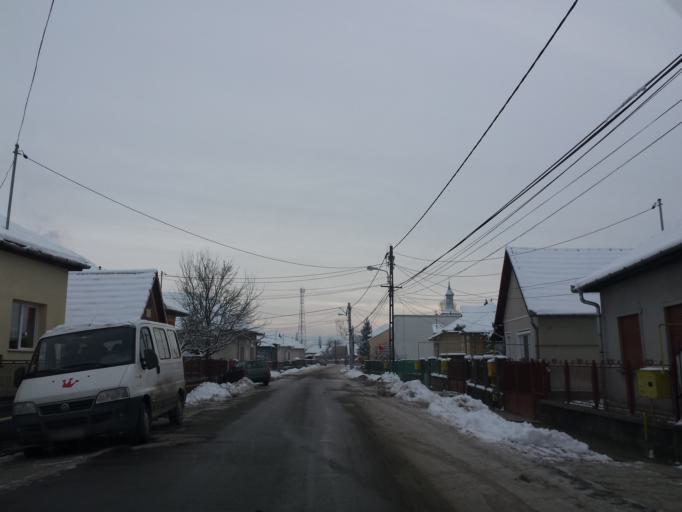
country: RO
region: Hunedoara
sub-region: Municipiul Deva
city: Cristur
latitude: 45.8272
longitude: 22.9413
